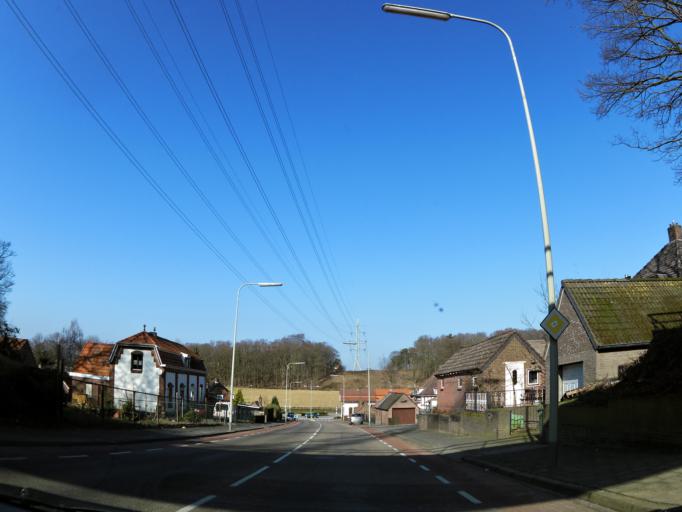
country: NL
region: Limburg
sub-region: Gemeente Heerlen
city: Heerlen
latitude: 50.8931
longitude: 6.0048
